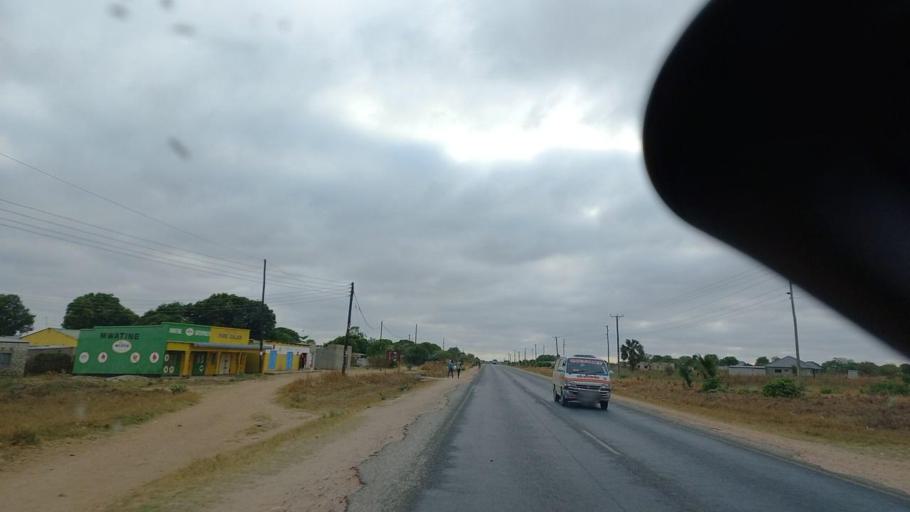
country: ZM
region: Lusaka
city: Chongwe
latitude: -15.3408
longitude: 28.6184
